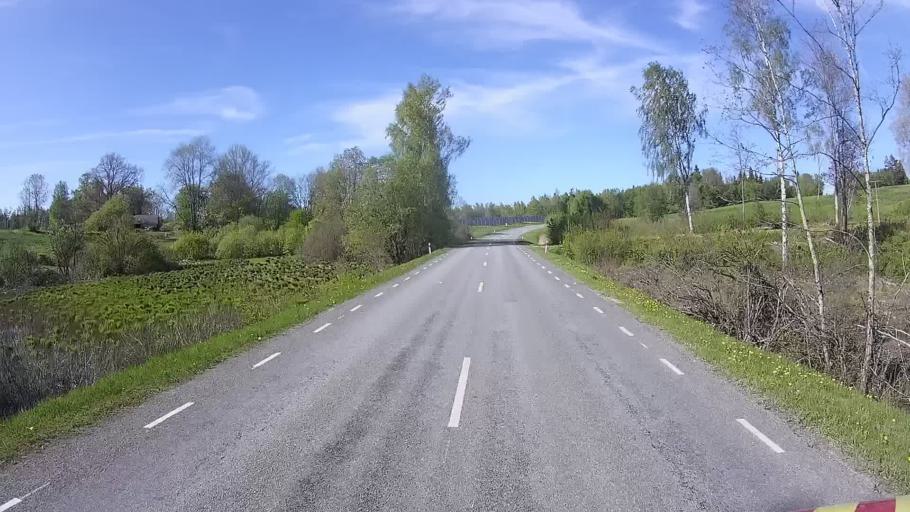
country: EE
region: Vorumaa
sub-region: Antsla vald
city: Vana-Antsla
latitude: 57.9771
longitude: 26.4657
